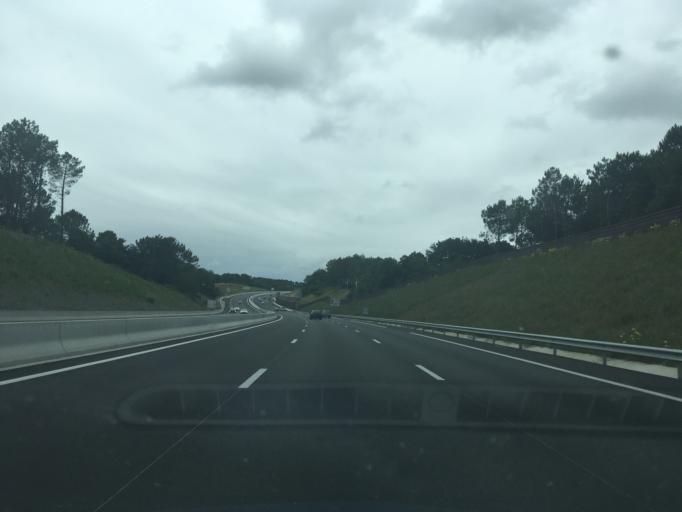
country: FR
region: Aquitaine
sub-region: Departement des Landes
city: Ondres
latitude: 43.5673
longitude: -1.4310
